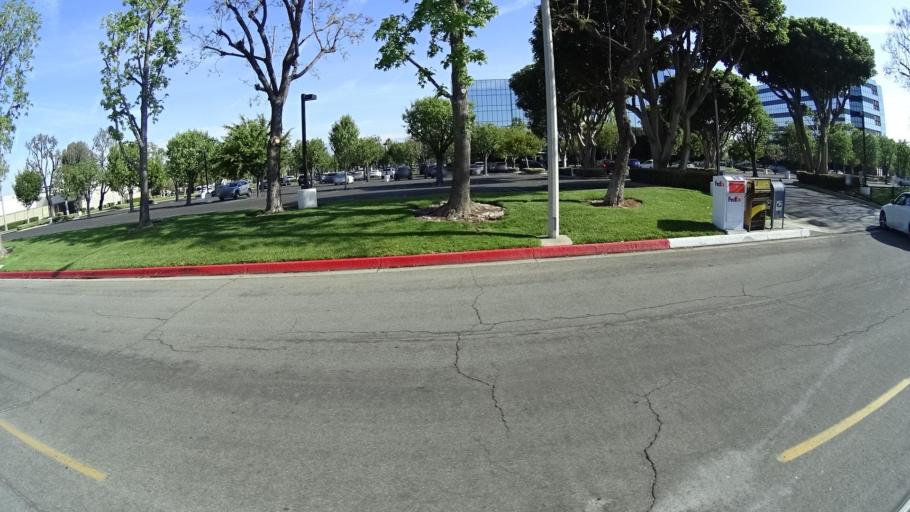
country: US
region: California
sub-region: Los Angeles County
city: Rowland Heights
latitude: 33.9913
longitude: -117.9169
